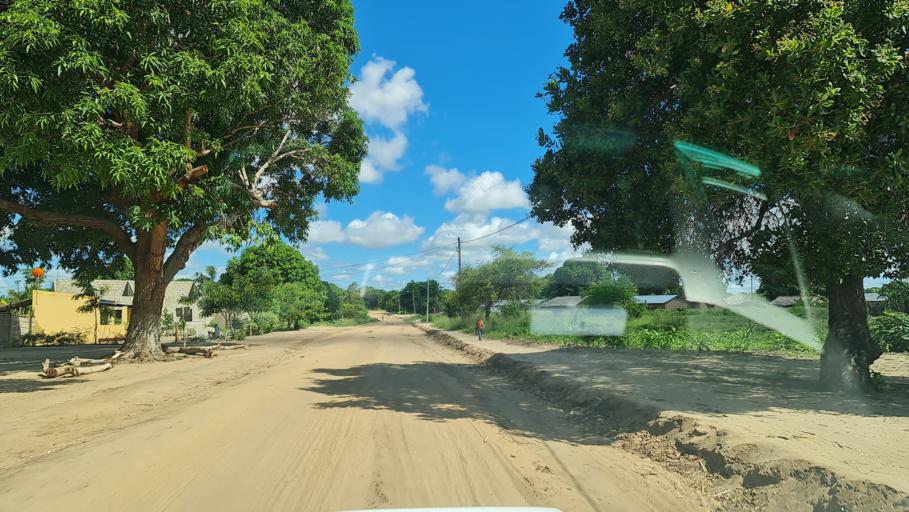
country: MZ
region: Nampula
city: Ilha de Mocambique
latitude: -15.5522
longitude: 40.4078
